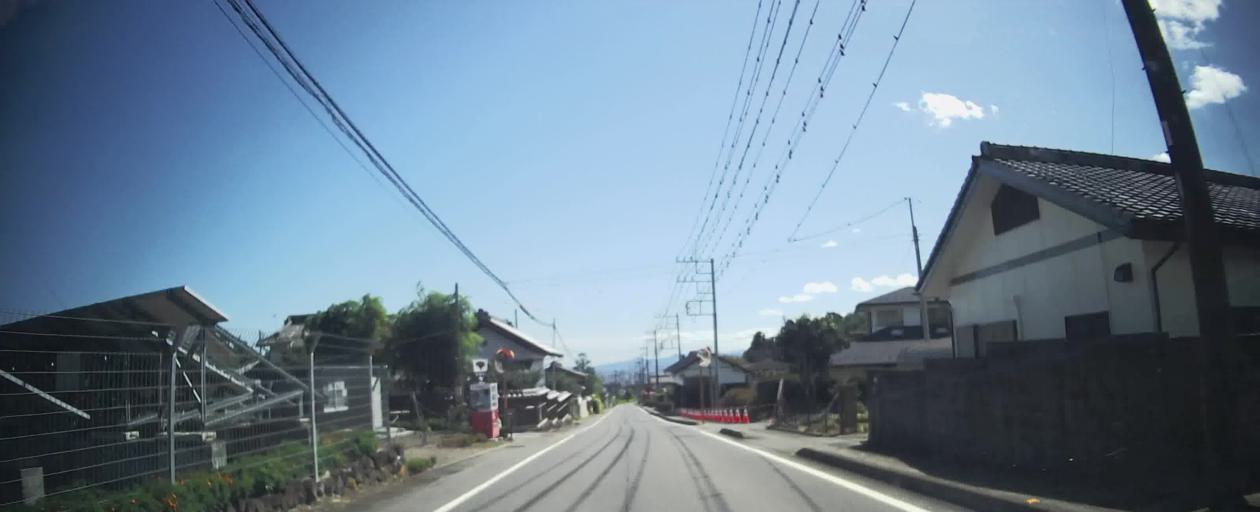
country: JP
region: Gunma
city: Kanekomachi
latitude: 36.4054
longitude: 138.9541
